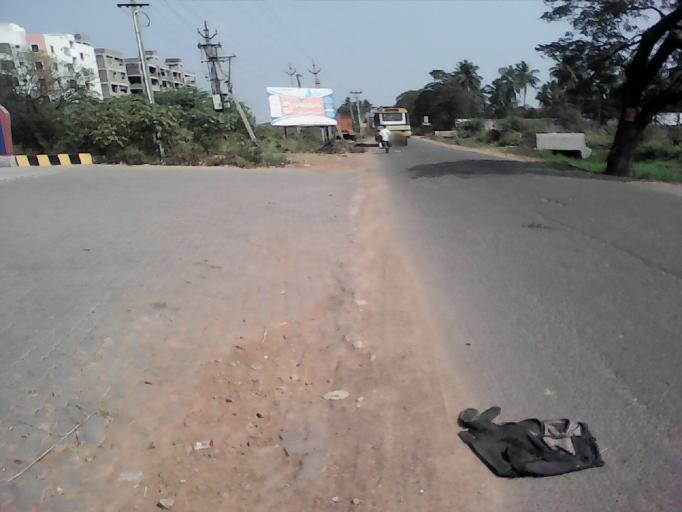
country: IN
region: Andhra Pradesh
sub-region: Guntur
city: Bhattiprolu
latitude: 16.2380
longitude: 80.6637
